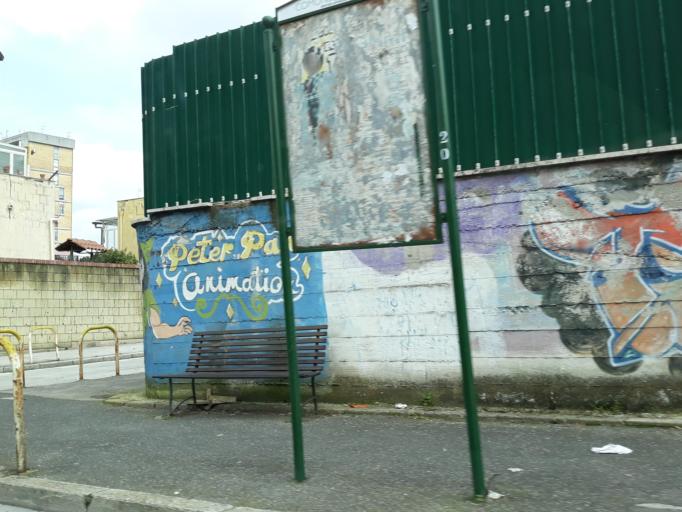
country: IT
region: Campania
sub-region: Provincia di Napoli
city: Melito di Napoli
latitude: 40.8908
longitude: 14.2339
